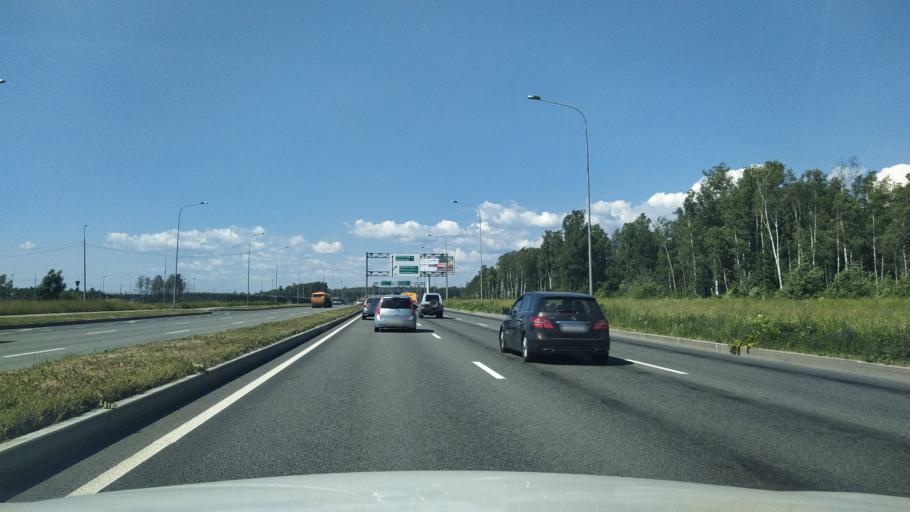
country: RU
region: St.-Petersburg
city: Levashovo
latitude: 60.0699
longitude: 30.1864
